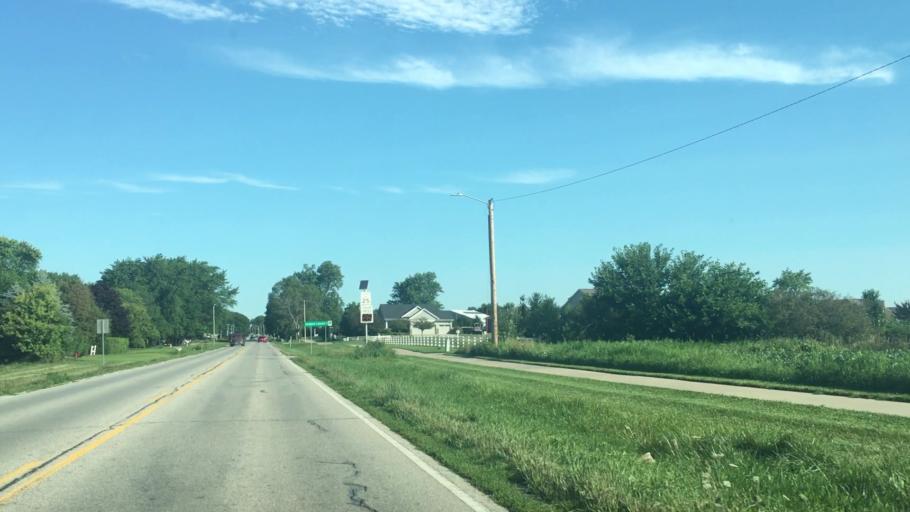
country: US
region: Iowa
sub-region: Johnson County
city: North Liberty
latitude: 41.7407
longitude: -91.5878
